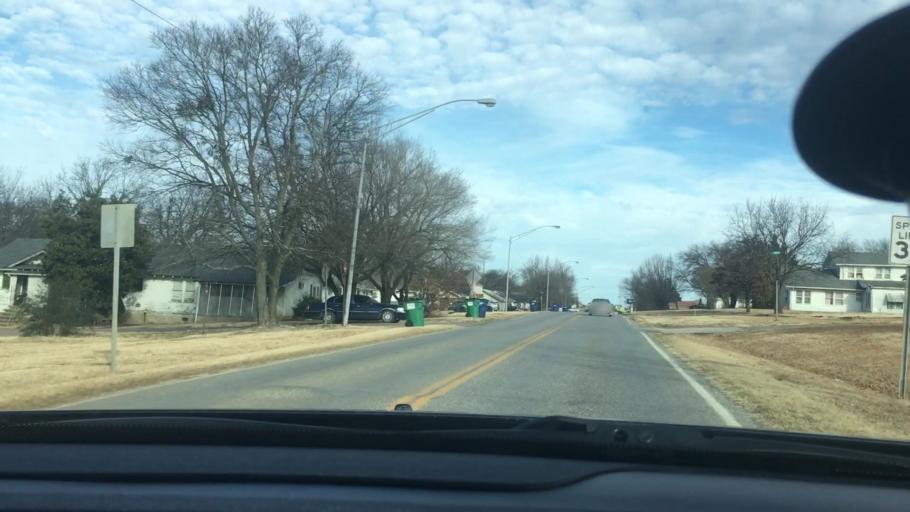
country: US
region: Oklahoma
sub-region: Seminole County
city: Konawa
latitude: 34.9521
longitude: -96.7521
